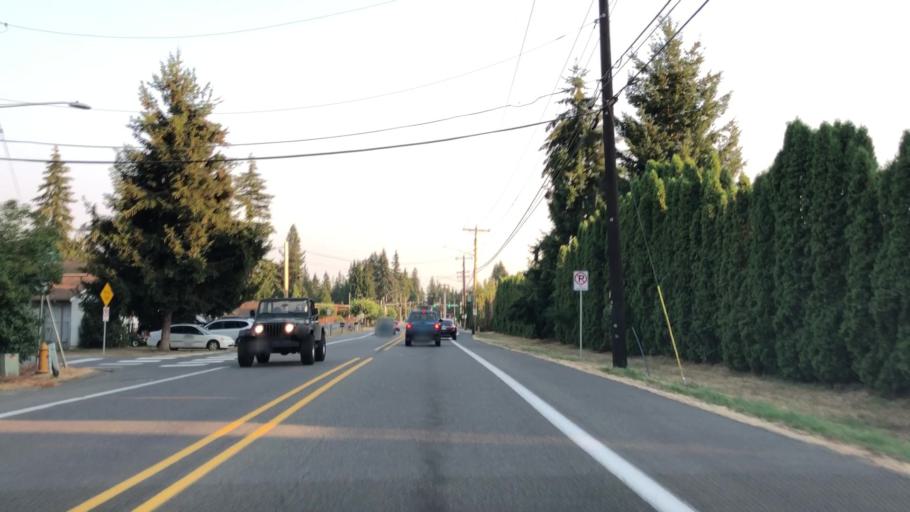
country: US
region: Washington
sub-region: Snohomish County
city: Smokey Point
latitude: 48.1207
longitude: -122.1626
